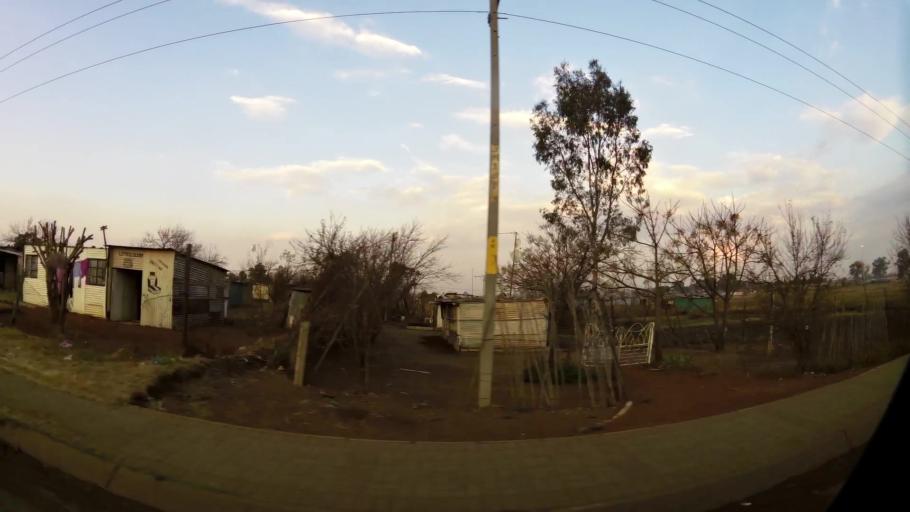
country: ZA
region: Gauteng
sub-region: City of Johannesburg Metropolitan Municipality
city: Orange Farm
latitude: -26.5408
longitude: 27.8444
